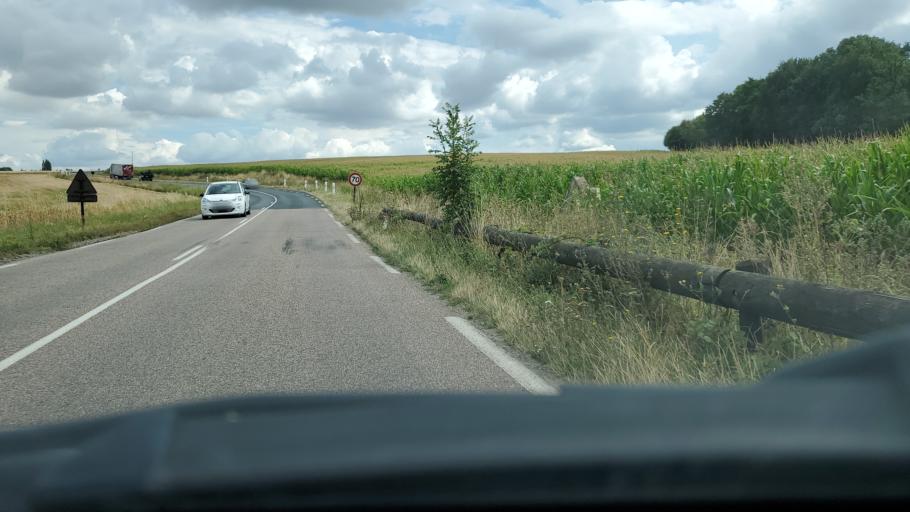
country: FR
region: Ile-de-France
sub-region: Departement de Seine-et-Marne
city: Bouleurs
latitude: 48.9011
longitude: 2.9357
